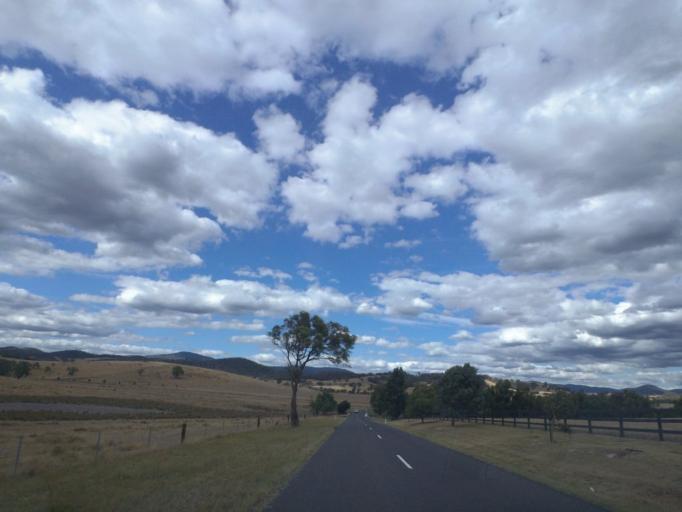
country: AU
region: Victoria
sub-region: Yarra Ranges
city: Yarra Glen
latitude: -37.6377
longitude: 145.4327
